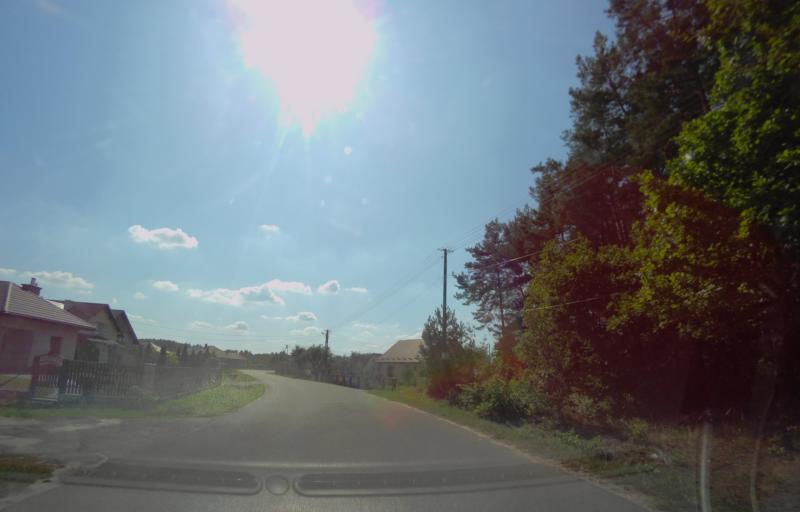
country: PL
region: Subcarpathian Voivodeship
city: Nowa Sarzyna
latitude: 50.3077
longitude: 22.3278
